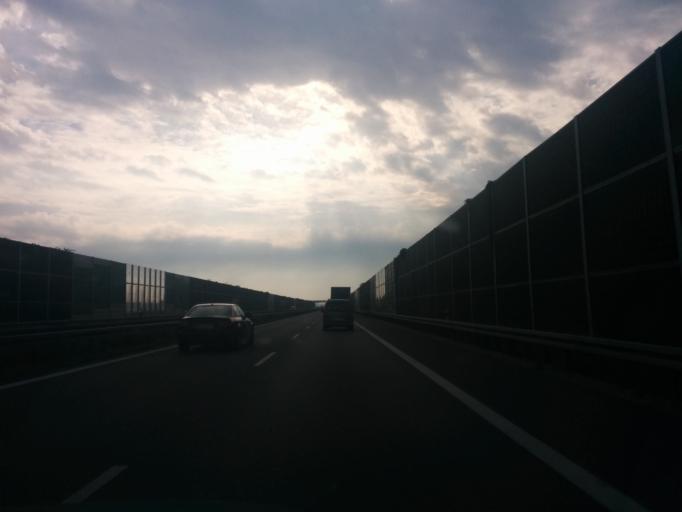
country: PL
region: Masovian Voivodeship
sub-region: Powiat bialobrzeski
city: Stara Blotnica
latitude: 51.5481
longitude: 21.0483
